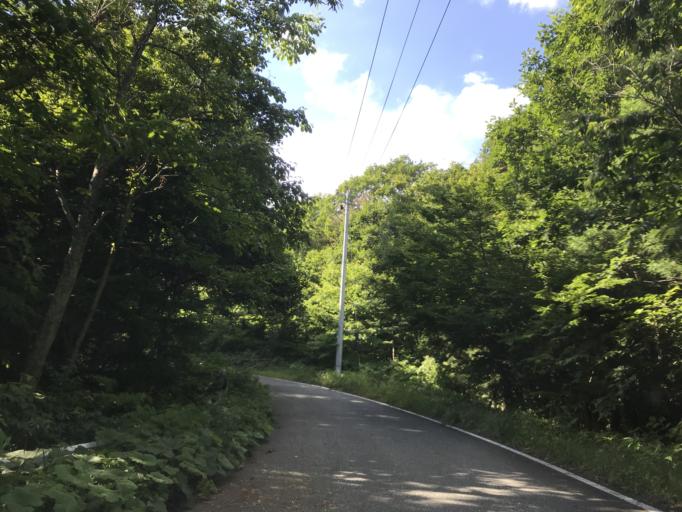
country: JP
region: Iwate
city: Ichinoseki
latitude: 38.8960
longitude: 140.8886
